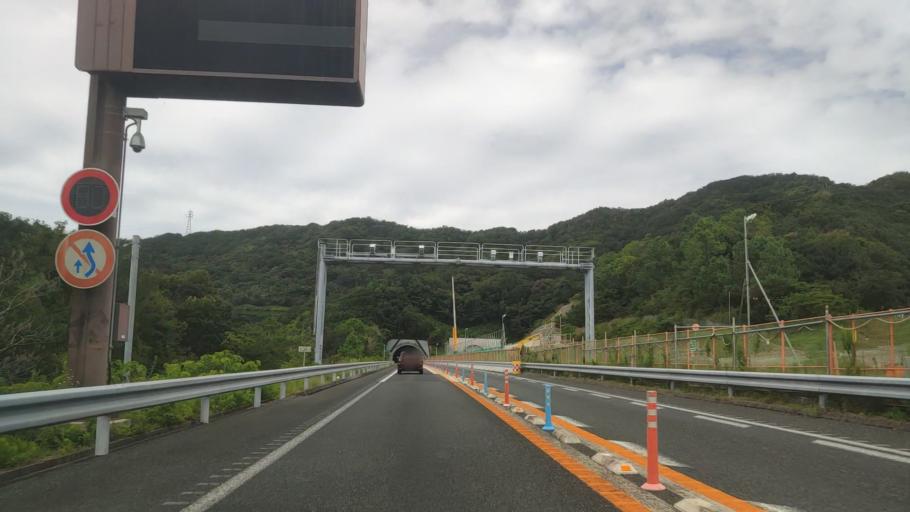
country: JP
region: Wakayama
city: Gobo
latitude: 33.8471
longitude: 135.2175
